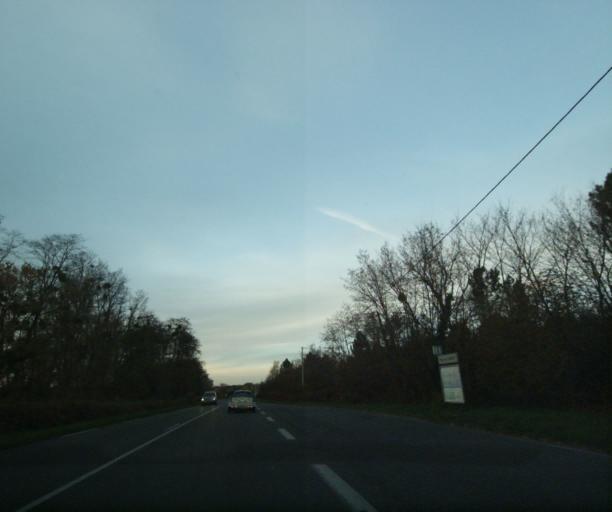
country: FR
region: Aquitaine
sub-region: Departement de la Gironde
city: Langon
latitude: 44.4959
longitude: -0.2364
